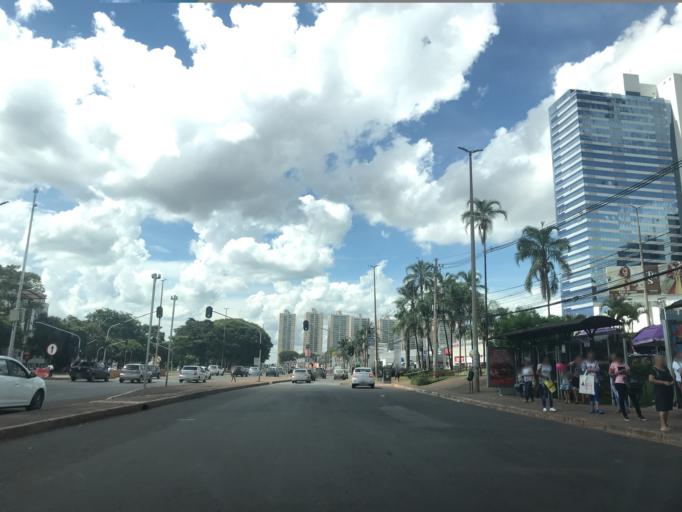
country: BR
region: Federal District
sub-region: Brasilia
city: Brasilia
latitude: -15.8424
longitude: -48.0454
